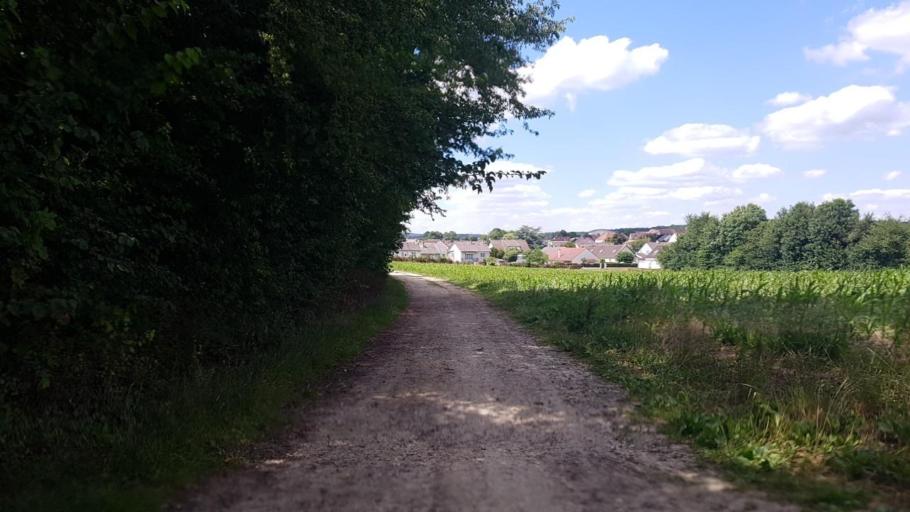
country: FR
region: Ile-de-France
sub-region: Departement de Seine-et-Marne
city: Moussy-le-Vieux
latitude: 49.0428
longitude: 2.6299
